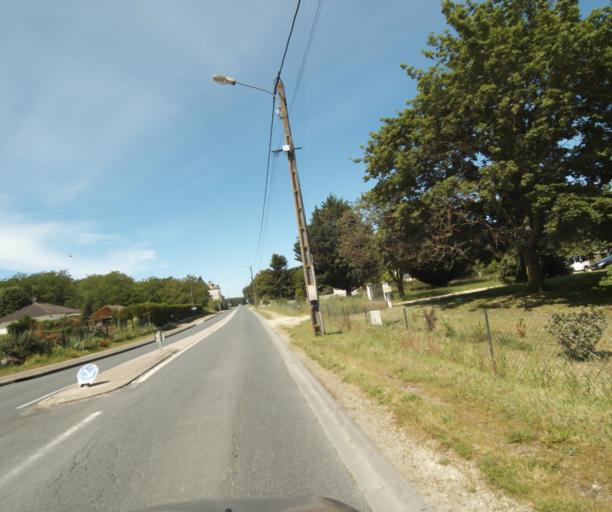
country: FR
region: Centre
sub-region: Departement d'Indre-et-Loire
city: Ligre
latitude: 47.1352
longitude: 0.3052
